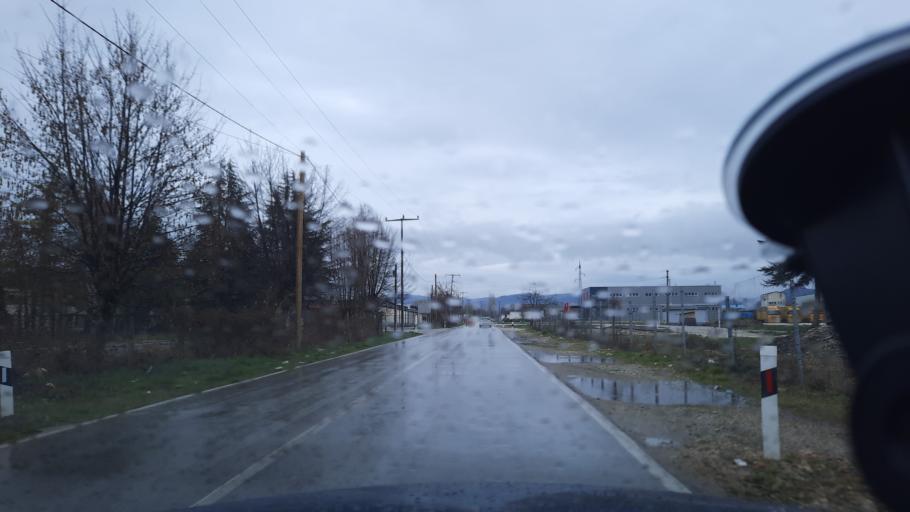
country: MK
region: Struga
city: Struga
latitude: 41.1980
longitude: 20.6773
